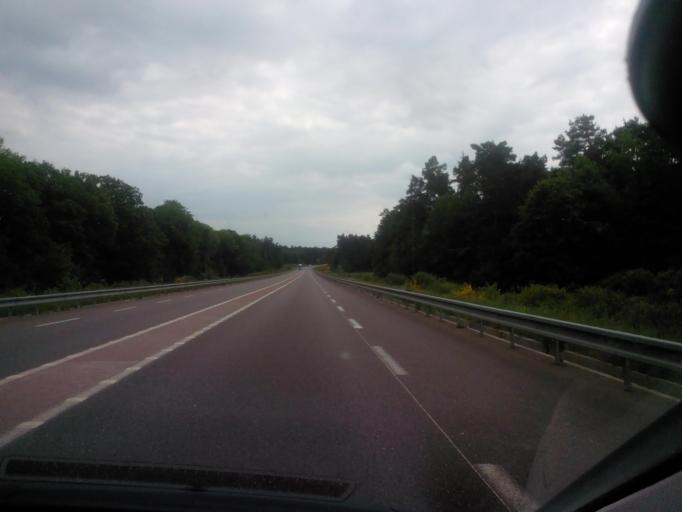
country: DE
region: Saarland
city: Uberherrn
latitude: 49.2139
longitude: 6.7255
